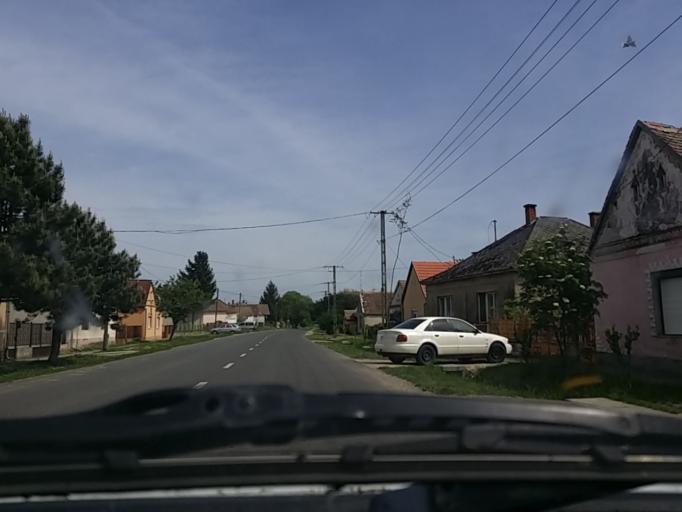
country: HU
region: Baranya
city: Vajszlo
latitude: 45.8556
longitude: 17.9945
